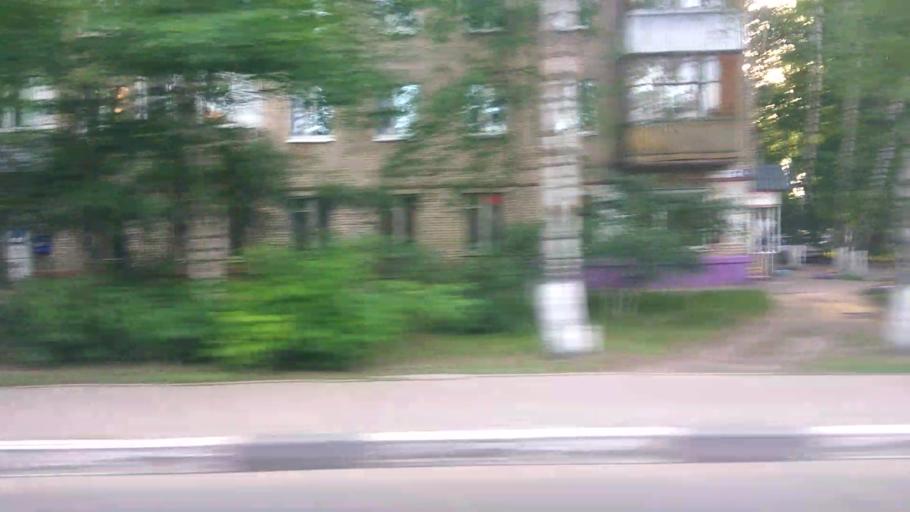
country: RU
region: Moskovskaya
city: Korolev
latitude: 55.9228
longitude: 37.7836
